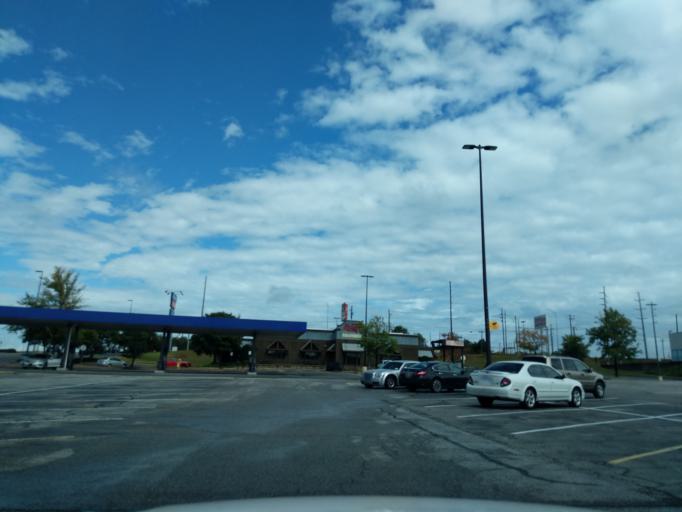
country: US
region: Alabama
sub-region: Tuscaloosa County
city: Tuscaloosa
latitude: 33.1668
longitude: -87.5190
